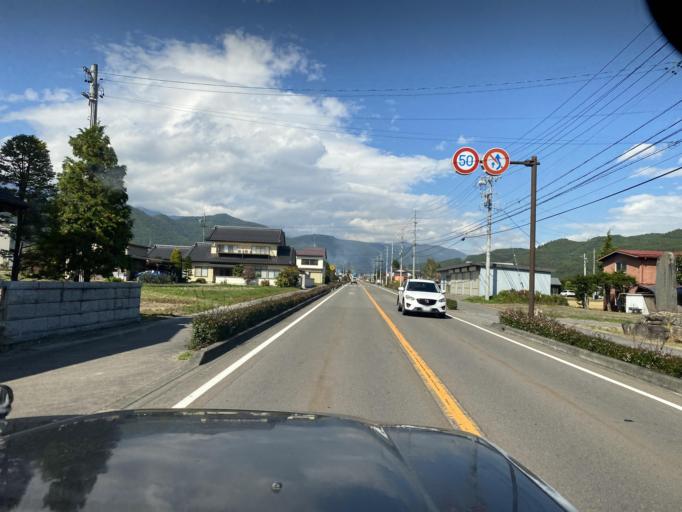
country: JP
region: Nagano
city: Omachi
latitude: 36.5238
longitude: 137.8515
